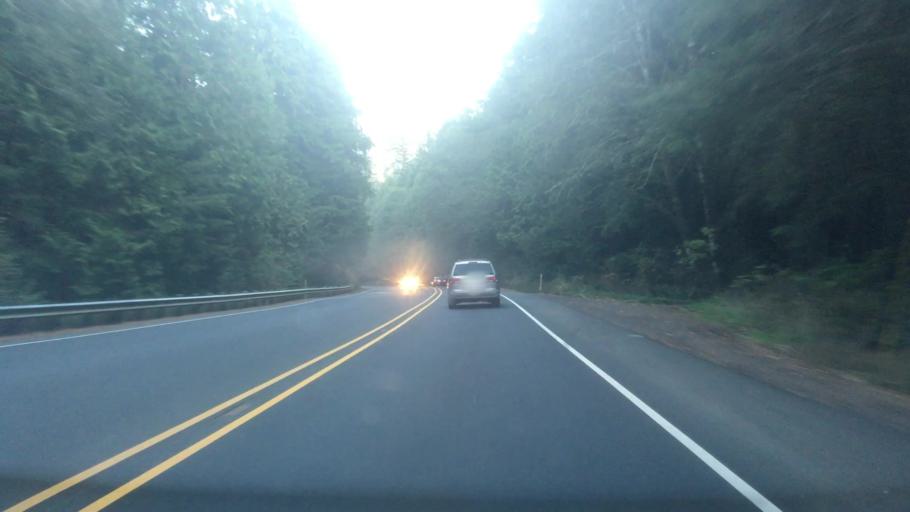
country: US
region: Oregon
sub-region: Clatsop County
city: Cannon Beach
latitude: 45.7795
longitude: -123.9536
